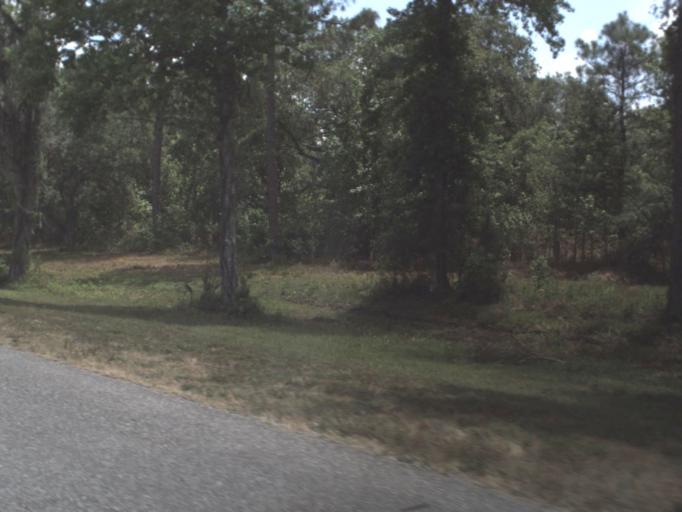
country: US
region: Florida
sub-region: Orange County
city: Christmas
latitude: 28.4524
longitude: -80.9981
